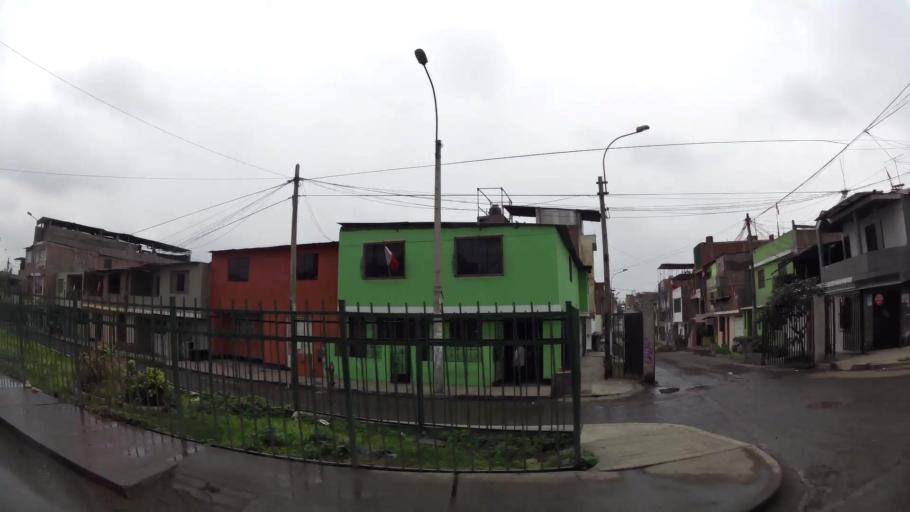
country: PE
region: Lima
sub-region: Lima
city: Surco
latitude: -12.1444
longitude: -76.9639
